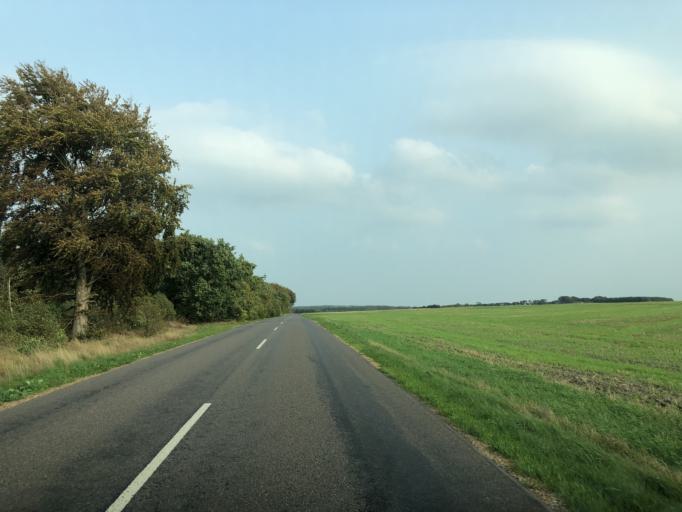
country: DK
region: Central Jutland
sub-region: Ringkobing-Skjern Kommune
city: Videbaek
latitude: 56.0527
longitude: 8.6954
